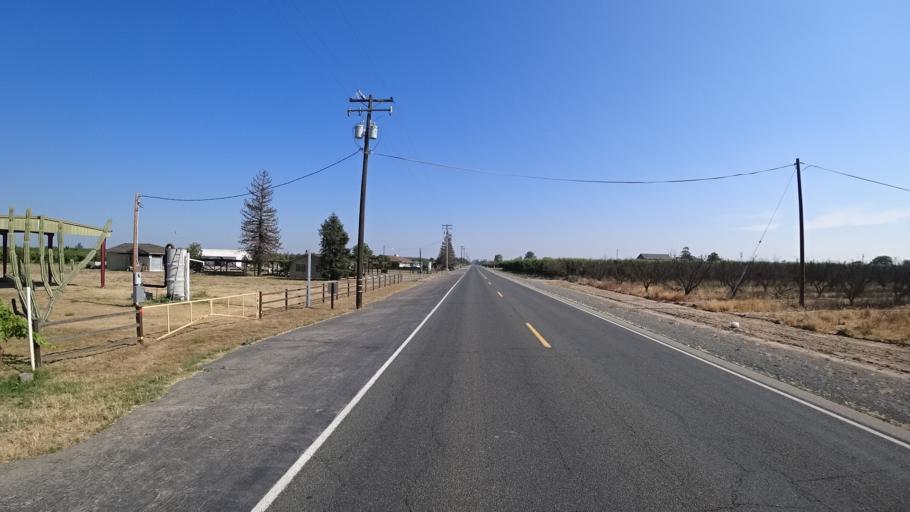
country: US
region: California
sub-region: Fresno County
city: Kingsburg
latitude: 36.4651
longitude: -119.5644
